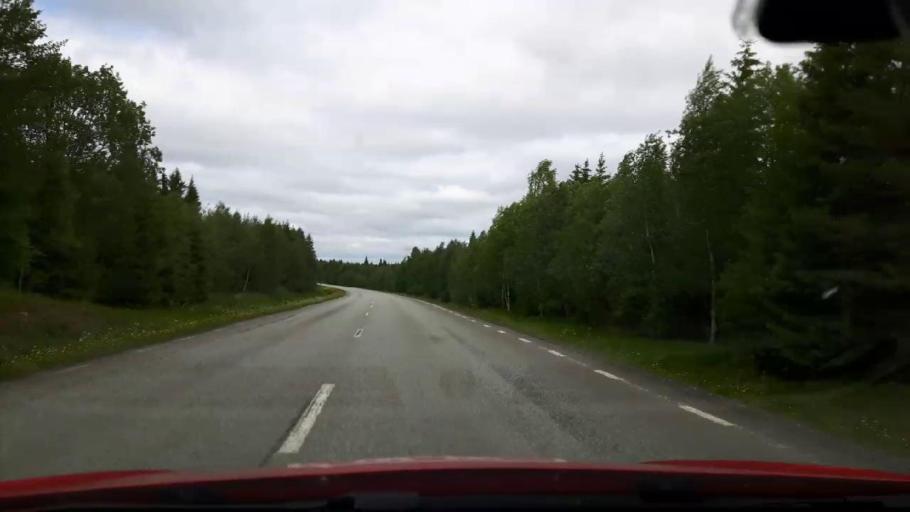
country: SE
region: Jaemtland
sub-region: Krokoms Kommun
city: Krokom
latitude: 63.3824
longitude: 14.5075
